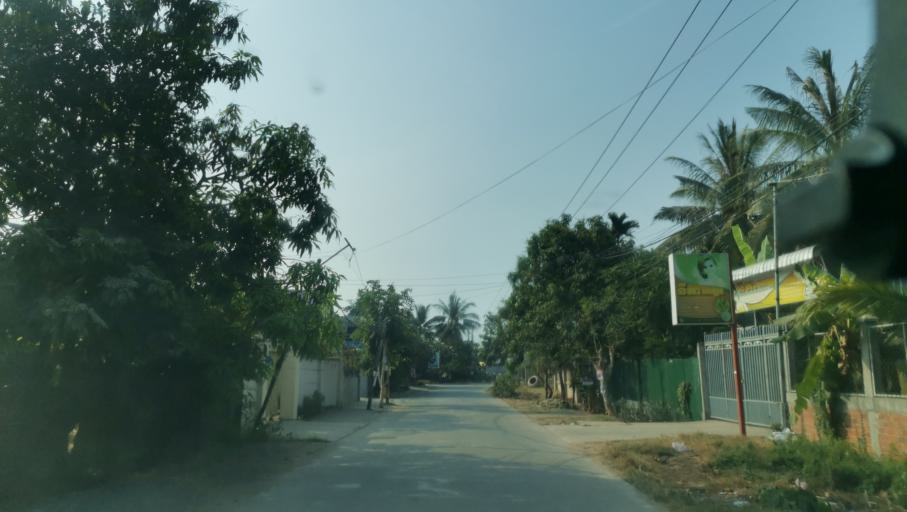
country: KH
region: Battambang
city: Battambang
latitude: 13.0867
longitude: 103.1932
